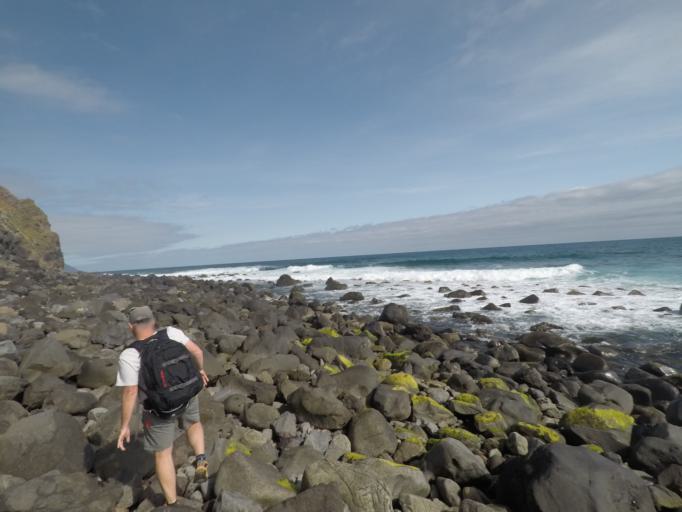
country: PT
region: Madeira
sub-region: Sao Vicente
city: Sao Vicente
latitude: 32.8301
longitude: -16.9876
